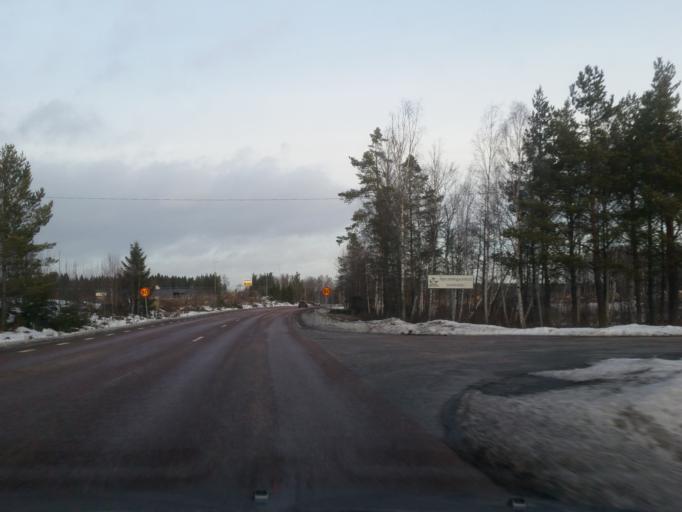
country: SE
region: Gaevleborg
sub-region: Sandvikens Kommun
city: Sandviken
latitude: 60.6289
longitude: 16.7506
